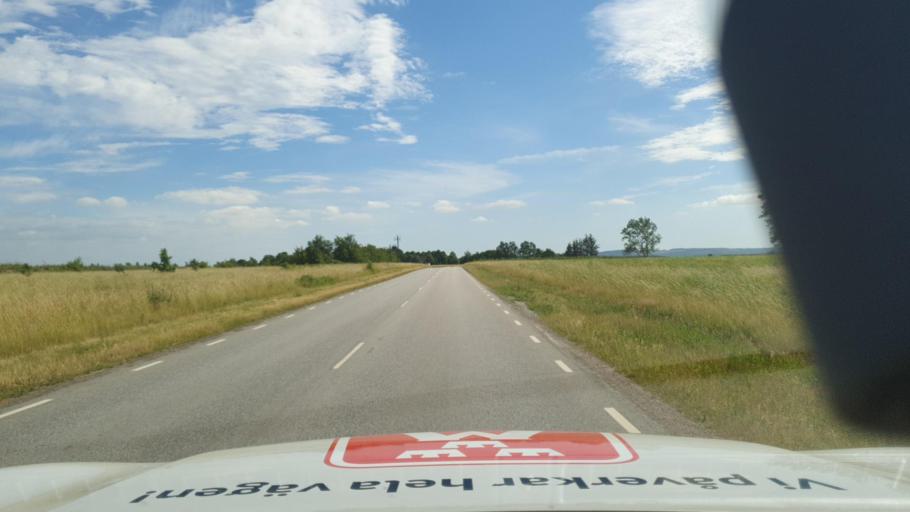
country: SE
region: Skane
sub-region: Sjobo Kommun
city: Sjoebo
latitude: 55.6230
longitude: 13.6545
